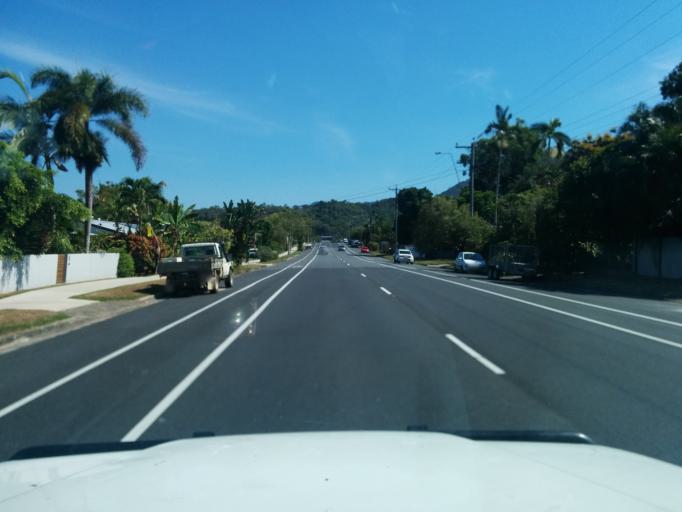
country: AU
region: Queensland
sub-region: Cairns
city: Redlynch
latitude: -16.9056
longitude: 145.7286
